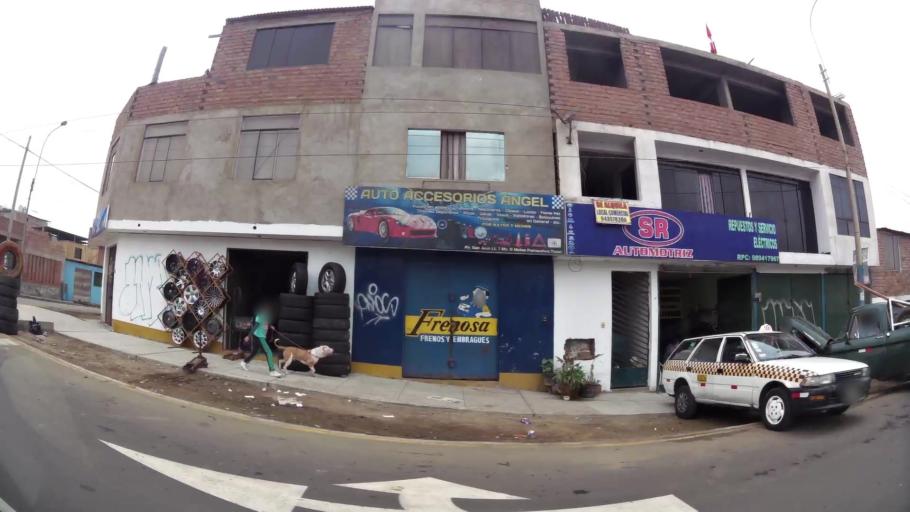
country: PE
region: Lima
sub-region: Lima
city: Surco
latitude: -12.1913
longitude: -76.9838
